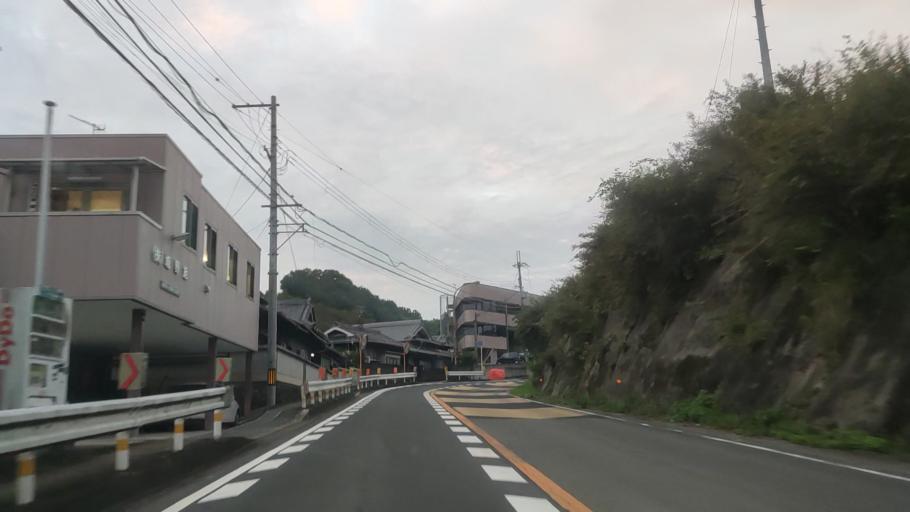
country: JP
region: Wakayama
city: Hashimoto
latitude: 34.3542
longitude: 135.6065
